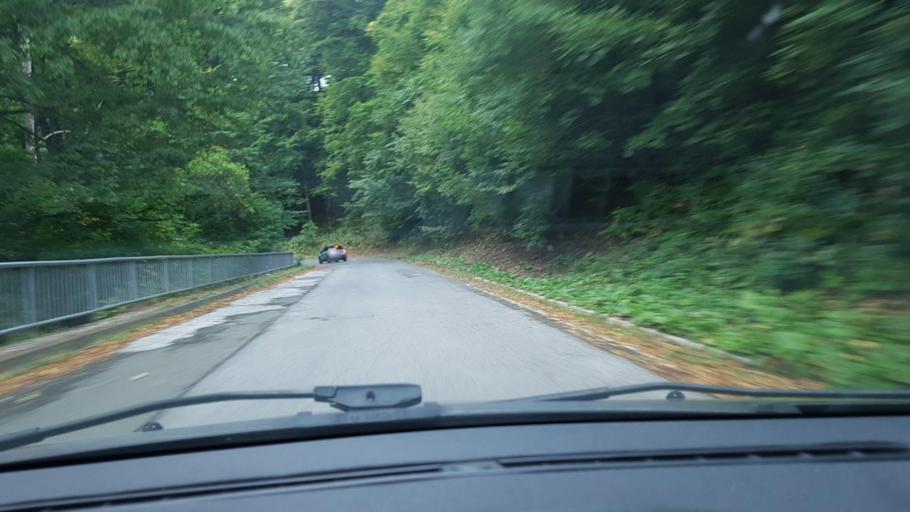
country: HR
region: Grad Zagreb
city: Kasina
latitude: 45.8903
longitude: 15.9372
